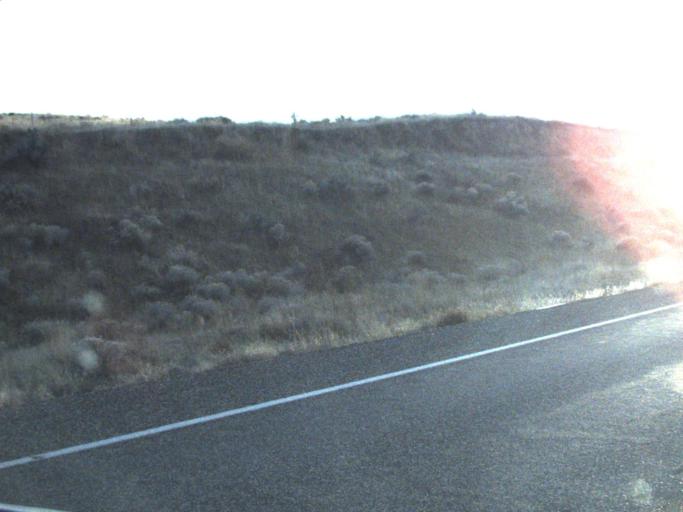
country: US
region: Washington
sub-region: Benton County
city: Finley
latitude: 46.0694
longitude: -118.8036
